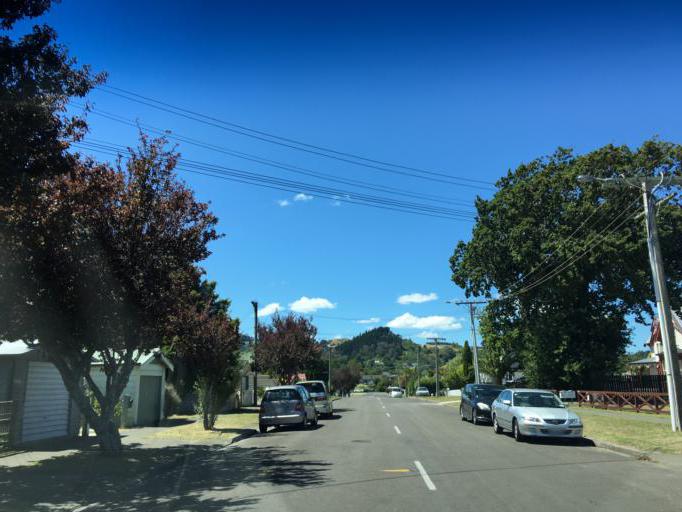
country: NZ
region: Gisborne
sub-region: Gisborne District
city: Gisborne
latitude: -38.6611
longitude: 178.0228
